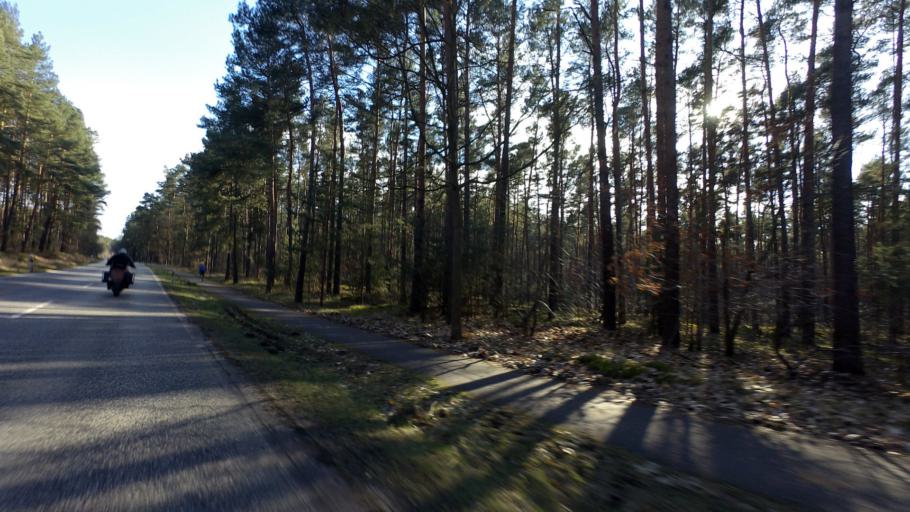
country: DE
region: Brandenburg
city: Oranienburg
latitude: 52.7238
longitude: 13.2671
